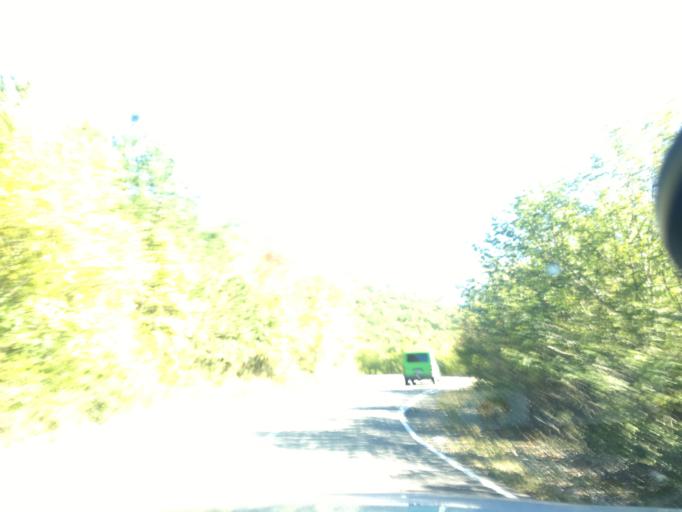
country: GE
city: Didi Lilo
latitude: 41.8587
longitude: 44.8997
